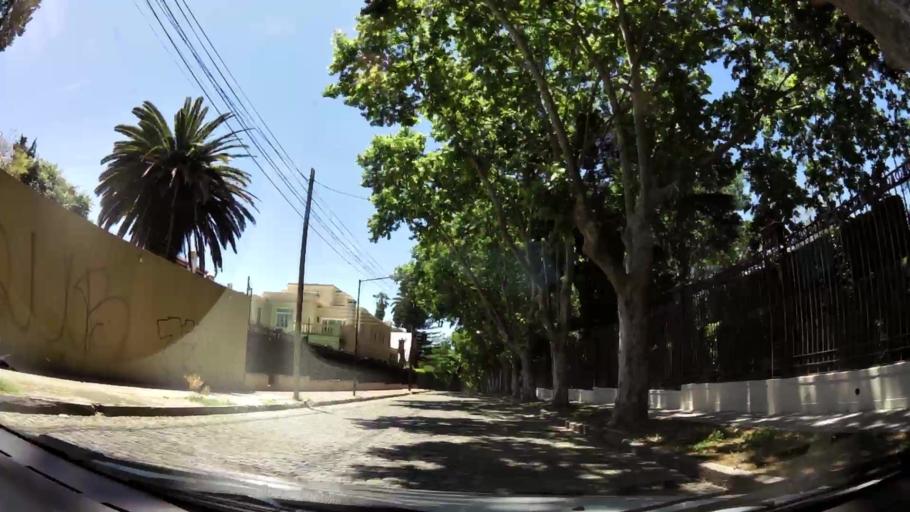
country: AR
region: Buenos Aires
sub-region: Partido de Vicente Lopez
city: Olivos
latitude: -34.4862
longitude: -58.4840
